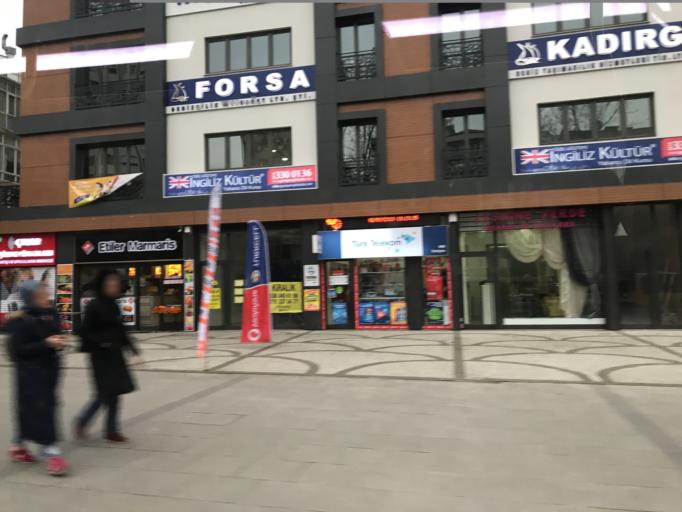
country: TR
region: Istanbul
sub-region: Atasehir
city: Atasehir
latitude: 40.9829
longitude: 29.0643
